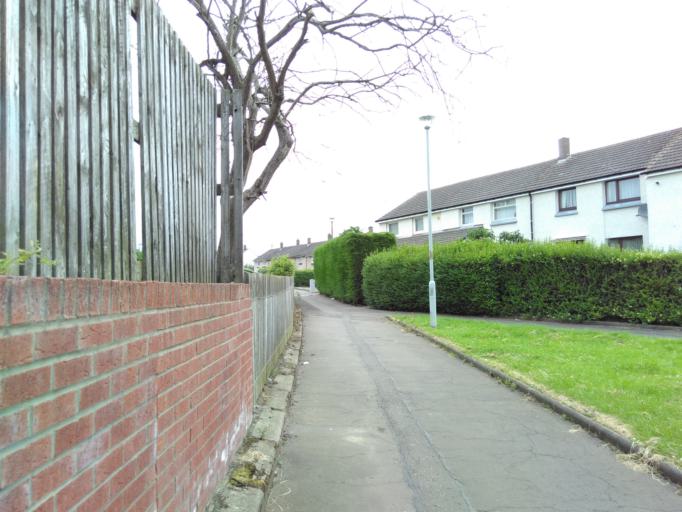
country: GB
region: Scotland
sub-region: Midlothian
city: Loanhead
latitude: 55.9155
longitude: -3.1409
